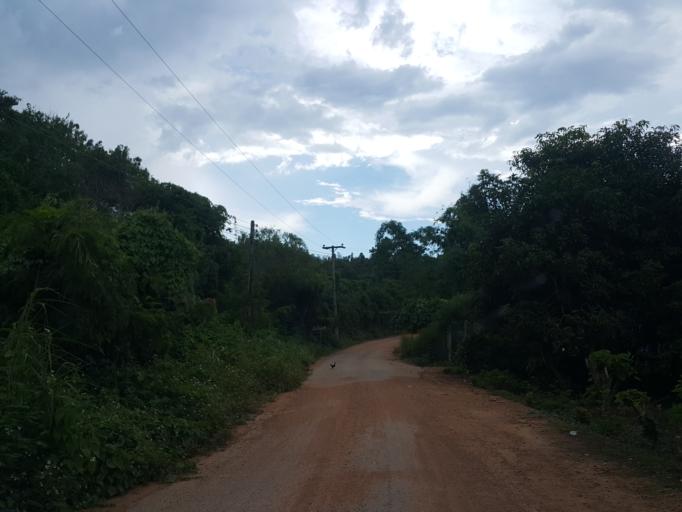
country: TH
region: Chiang Mai
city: Phrao
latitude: 19.3288
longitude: 99.1484
